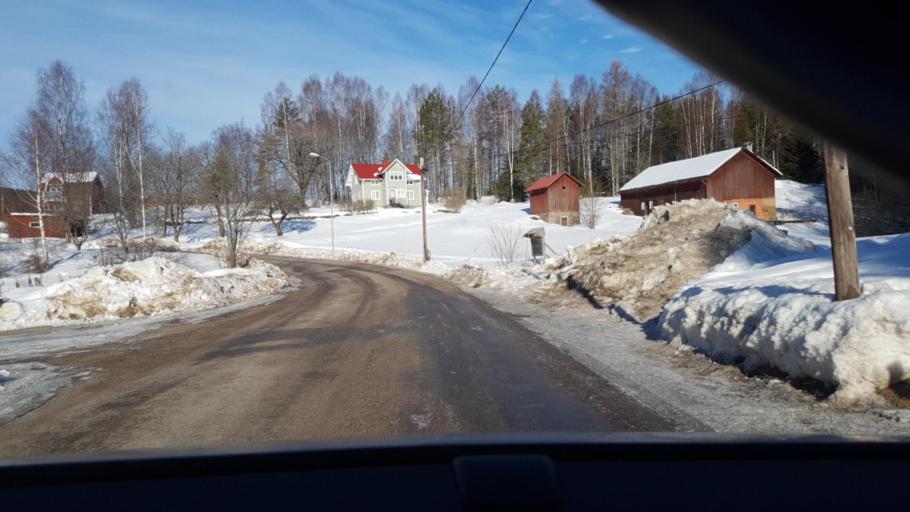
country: NO
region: Hedmark
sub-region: Eidskog
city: Skotterud
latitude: 59.8186
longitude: 12.1513
